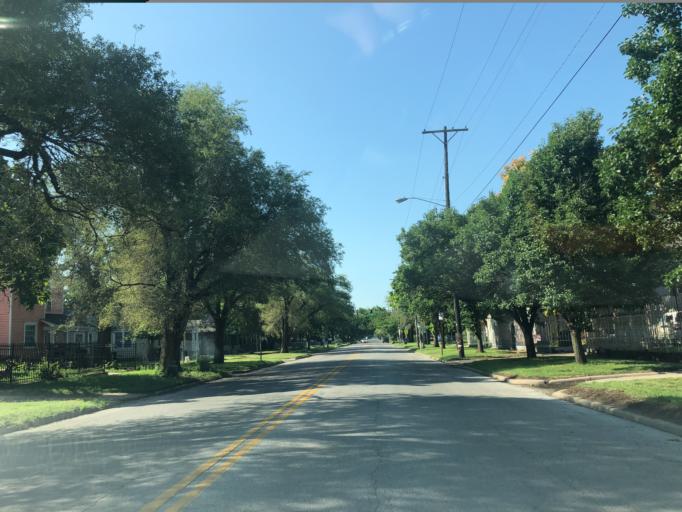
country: US
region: Kansas
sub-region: Sedgwick County
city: Wichita
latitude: 37.7144
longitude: -97.3420
